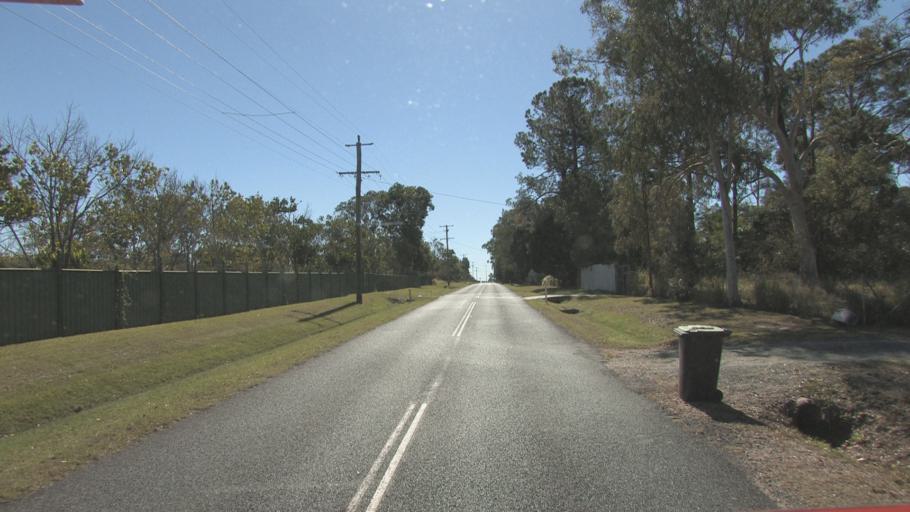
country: AU
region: Queensland
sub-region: Logan
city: Park Ridge South
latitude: -27.7106
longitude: 153.0587
